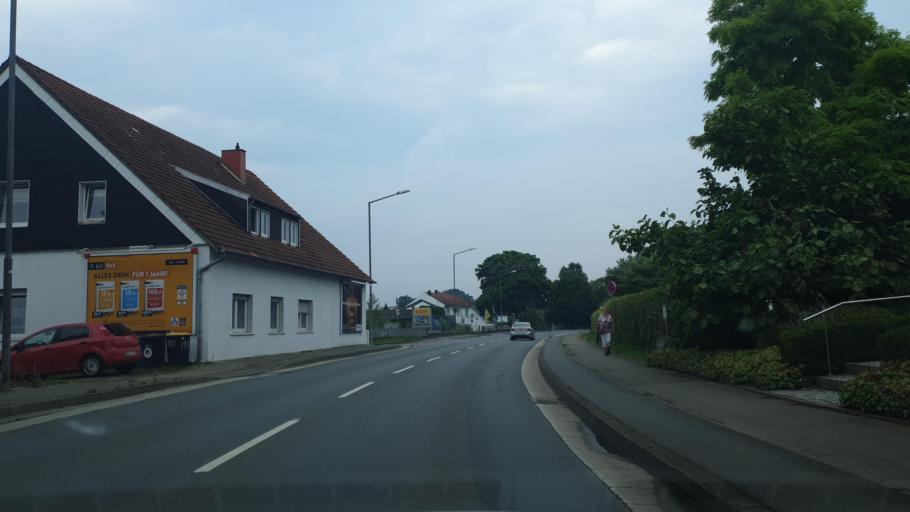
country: DE
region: North Rhine-Westphalia
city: Bad Oeynhausen
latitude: 52.2283
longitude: 8.7978
